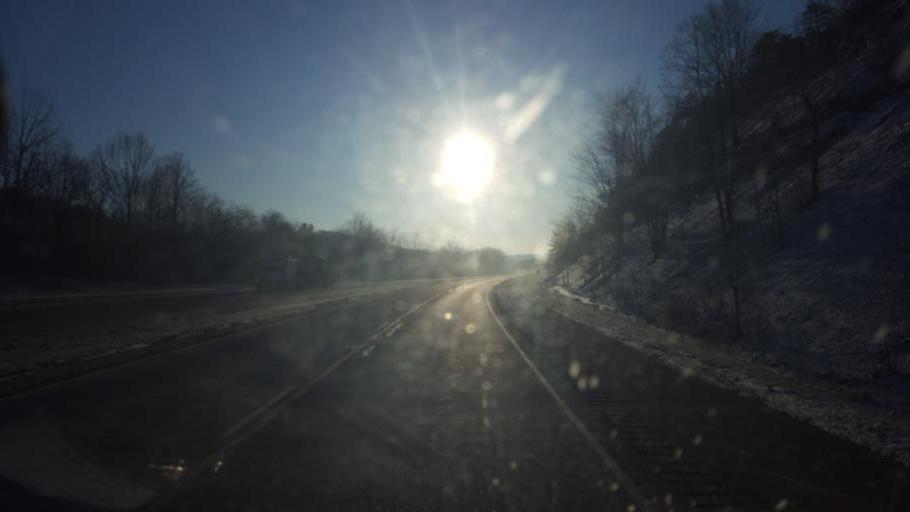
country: US
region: Ohio
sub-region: Pike County
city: Piketon
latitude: 39.0570
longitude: -83.0677
